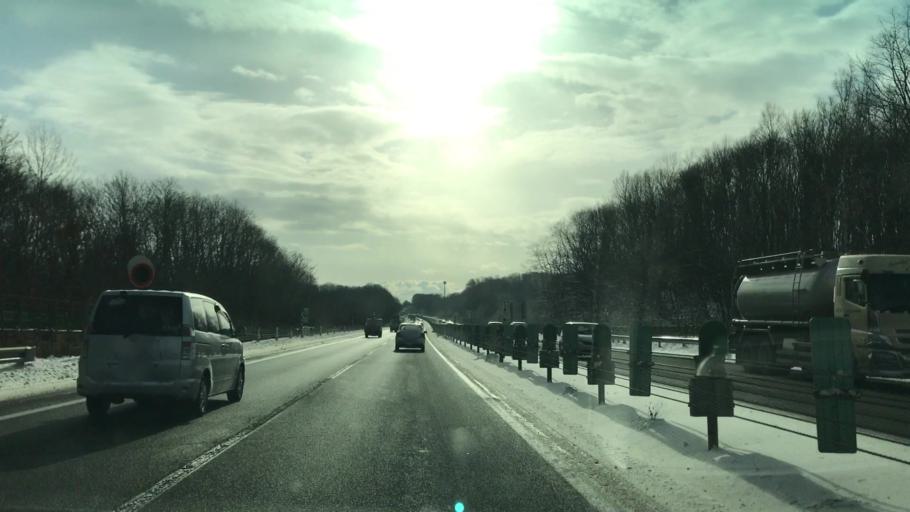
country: JP
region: Hokkaido
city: Kitahiroshima
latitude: 42.9458
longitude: 141.5175
